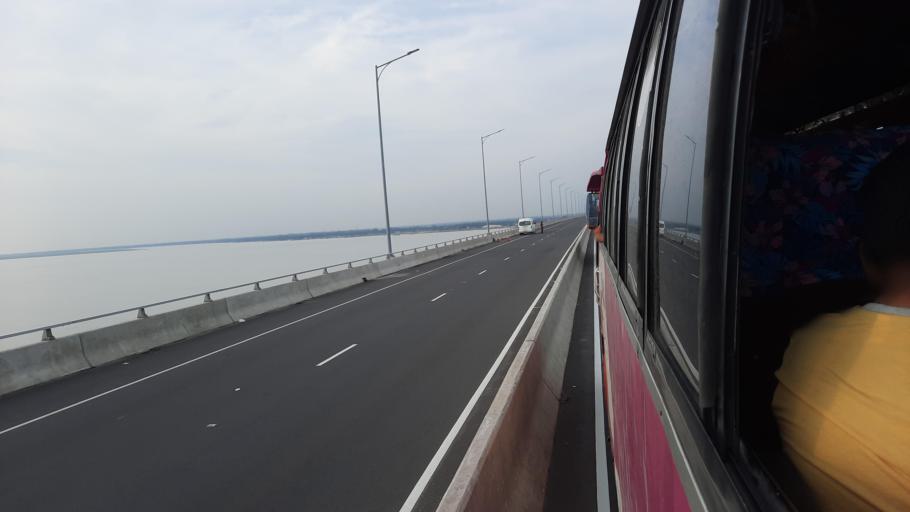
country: BD
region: Dhaka
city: Char Bhadrasan
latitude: 23.4506
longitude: 90.2615
